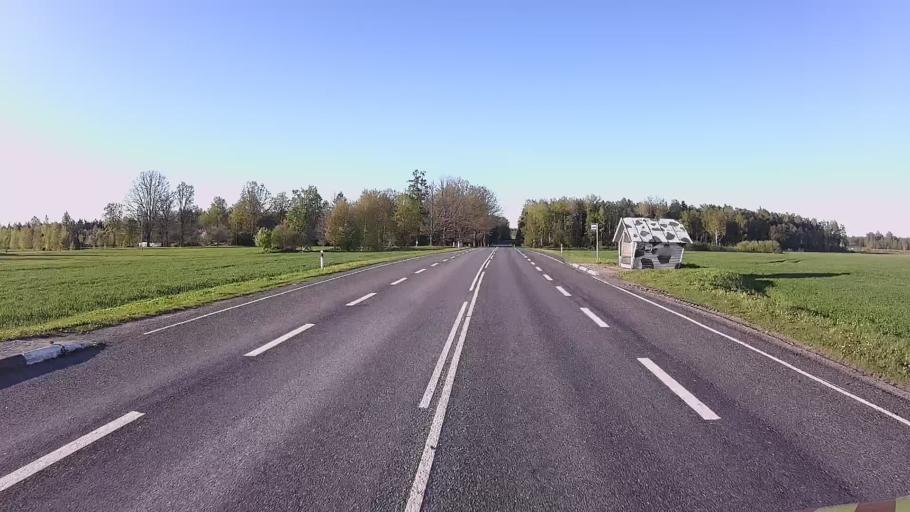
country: EE
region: Jogevamaa
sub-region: Poltsamaa linn
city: Poltsamaa
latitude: 58.5229
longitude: 25.8699
